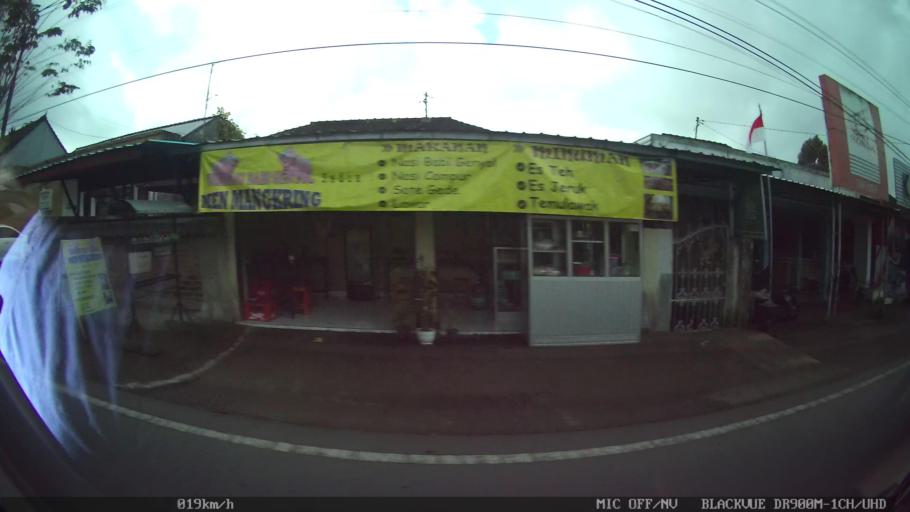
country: ID
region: Bali
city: Petang
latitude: -8.4049
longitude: 115.2191
